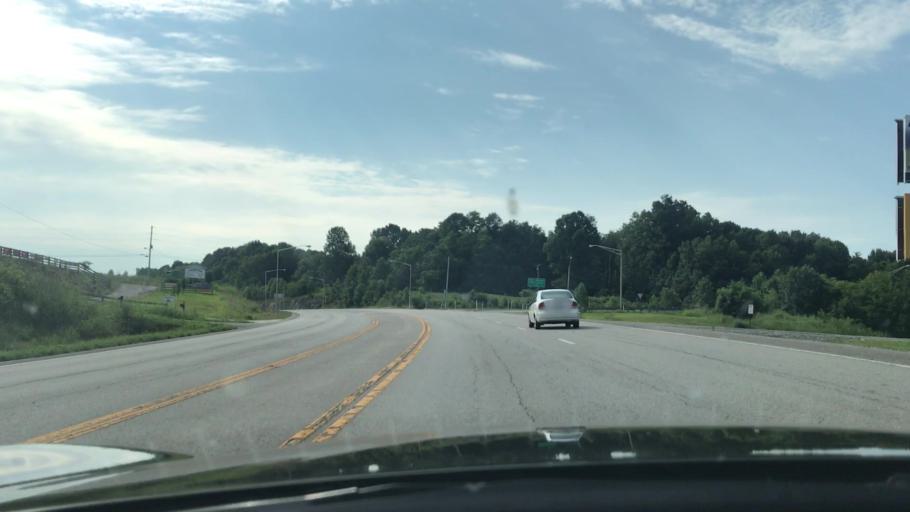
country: US
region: Kentucky
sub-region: Green County
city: Greensburg
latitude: 37.2748
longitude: -85.5094
